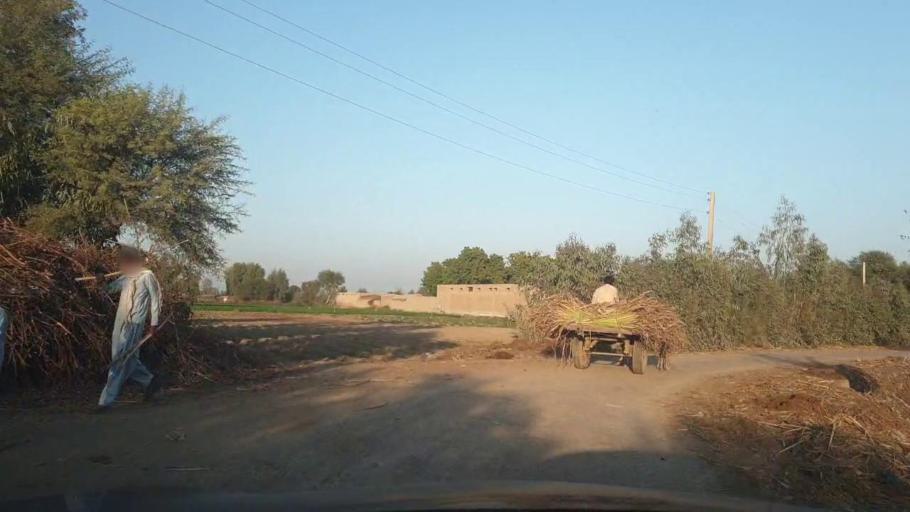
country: PK
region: Sindh
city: Ubauro
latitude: 28.1715
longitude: 69.5834
